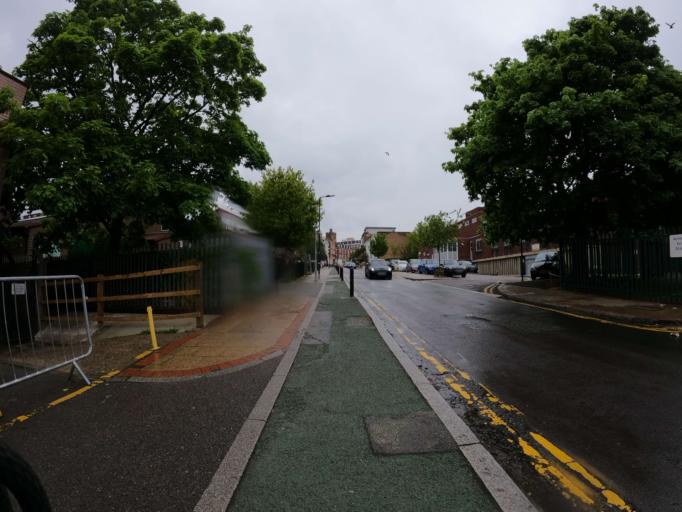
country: GB
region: England
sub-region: Greater London
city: Acton
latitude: 51.5058
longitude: -0.2702
